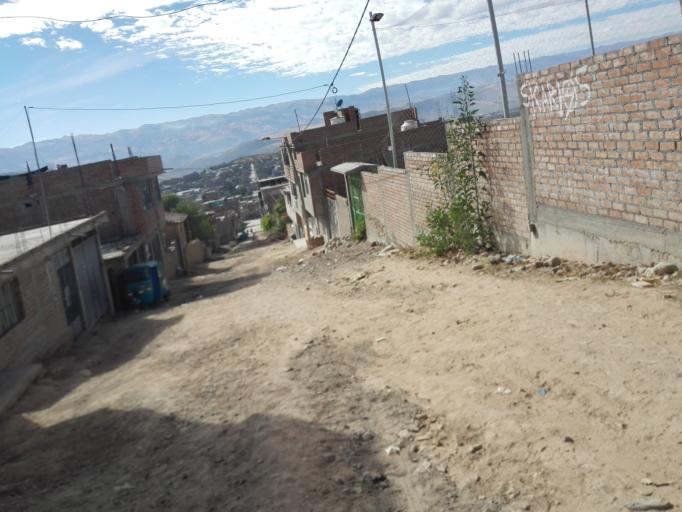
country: PE
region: Ayacucho
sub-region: Provincia de Huamanga
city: Ayacucho
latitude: -13.1387
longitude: -74.2345
